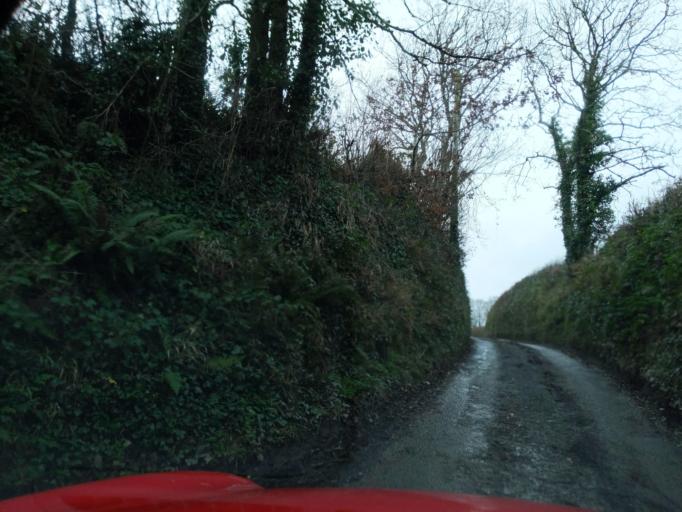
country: GB
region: England
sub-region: Cornwall
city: Fowey
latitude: 50.3378
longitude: -4.5818
